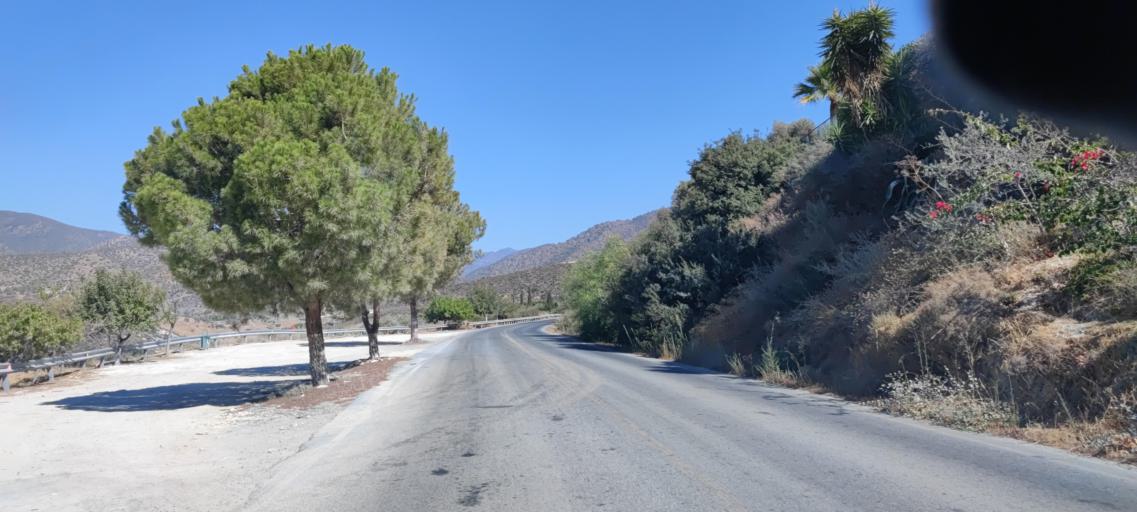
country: CY
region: Limassol
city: Mouttagiaka
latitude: 34.7455
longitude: 33.0911
